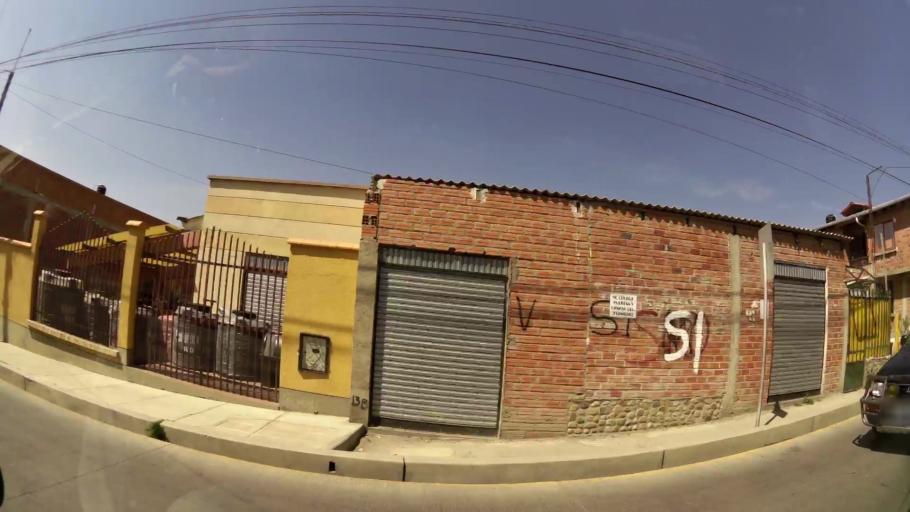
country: BO
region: La Paz
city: La Paz
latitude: -16.5317
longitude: -68.1266
